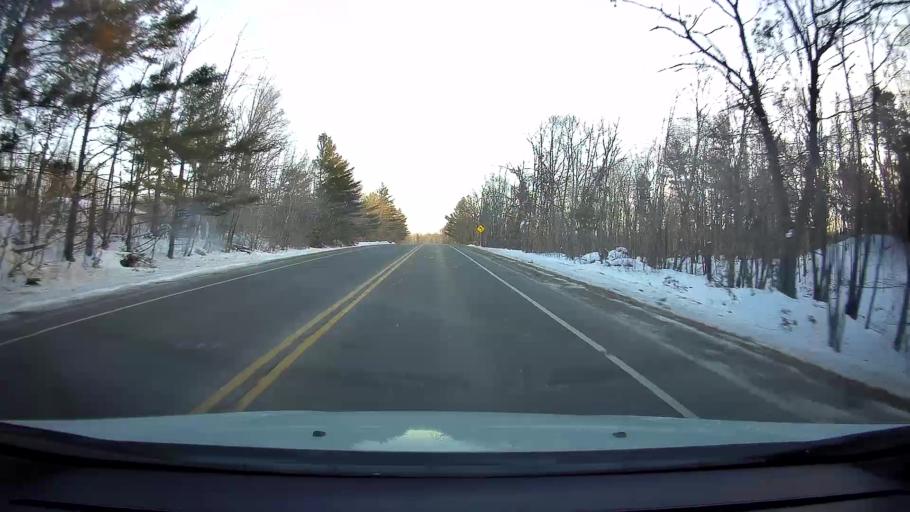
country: US
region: Wisconsin
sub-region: Barron County
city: Turtle Lake
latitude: 45.4468
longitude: -92.1126
